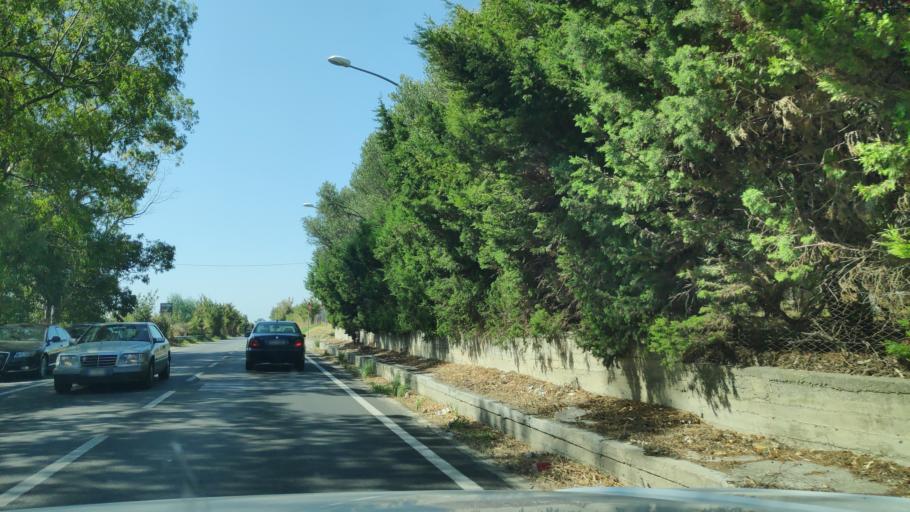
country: IT
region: Calabria
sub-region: Provincia di Reggio Calabria
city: Bianco
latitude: 38.1195
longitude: 16.1588
